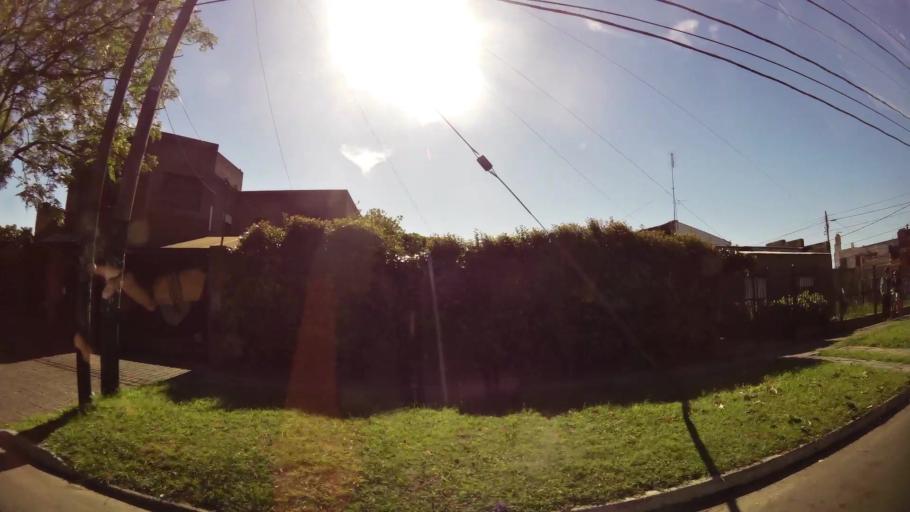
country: AR
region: Buenos Aires
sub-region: Partido de Lomas de Zamora
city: Lomas de Zamora
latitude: -34.7589
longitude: -58.4160
